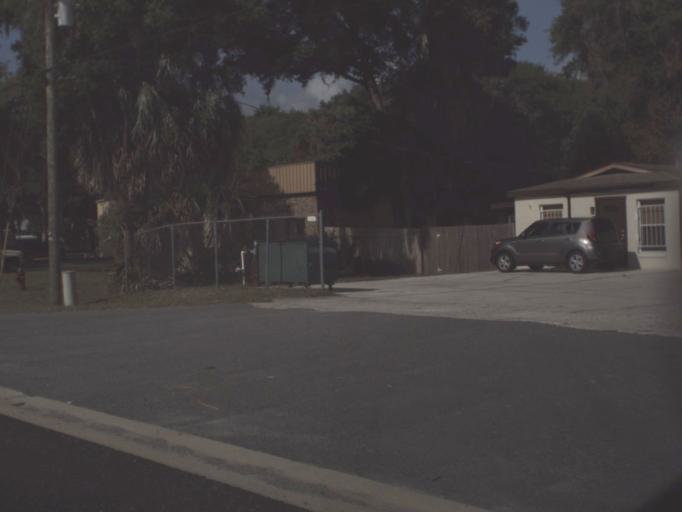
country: US
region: Florida
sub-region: Lake County
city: Fruitland Park
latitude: 28.8753
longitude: -81.9066
